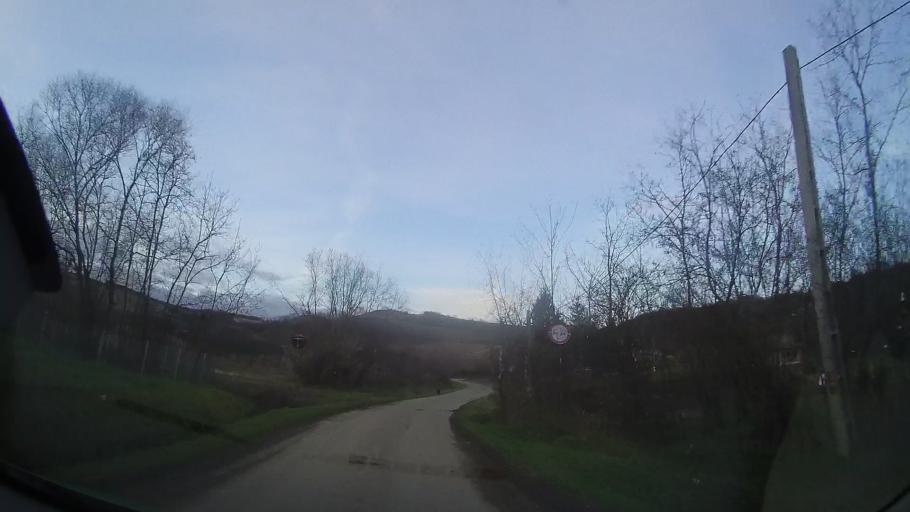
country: RO
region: Cluj
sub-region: Comuna Geaca
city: Geaca
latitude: 46.8545
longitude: 24.0469
